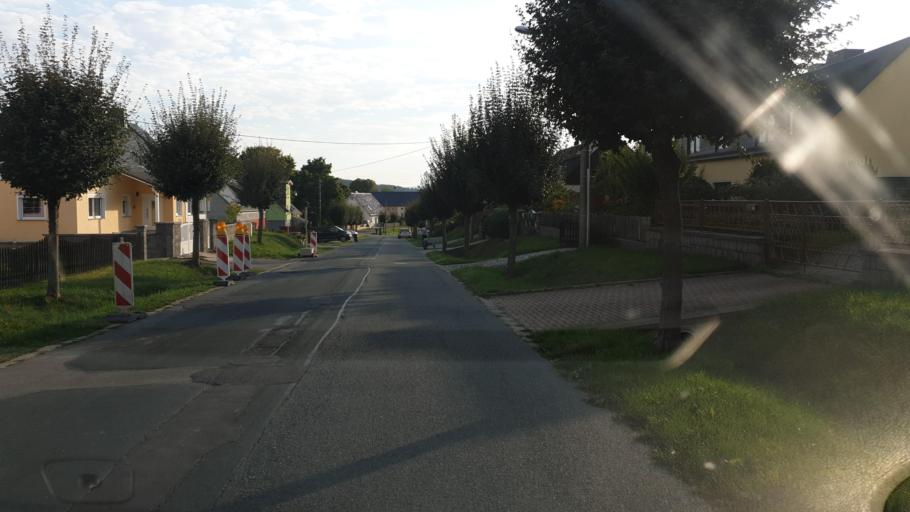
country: DE
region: Saxony
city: Lossnitz
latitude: 50.6220
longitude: 12.7443
